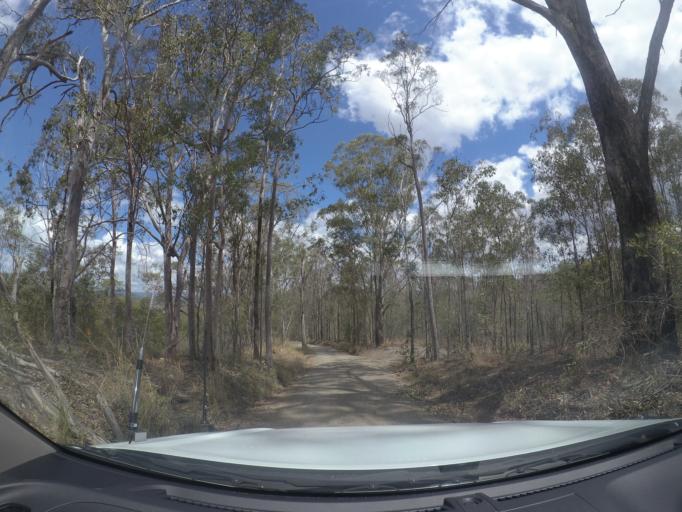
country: AU
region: Queensland
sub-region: Logan
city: Cedar Vale
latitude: -27.8962
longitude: 153.0437
